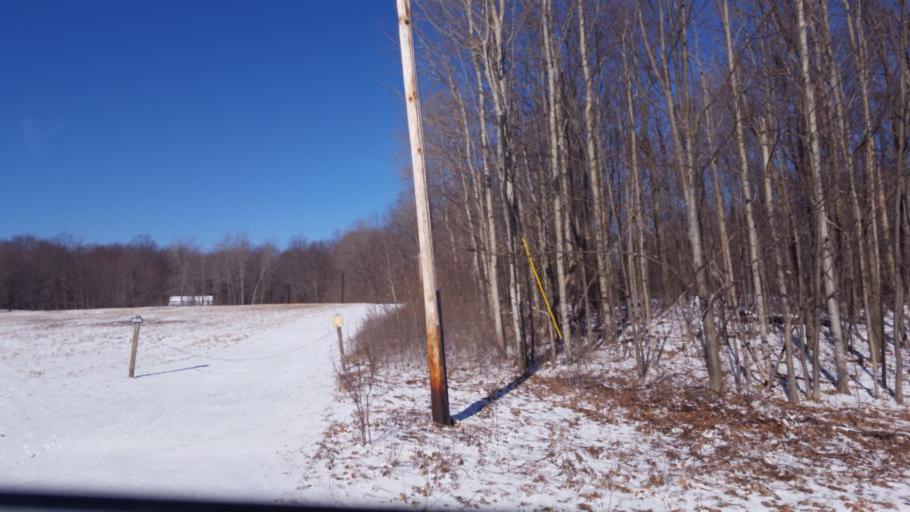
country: US
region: New York
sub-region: Allegany County
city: Wellsville
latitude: 42.1537
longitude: -77.9339
